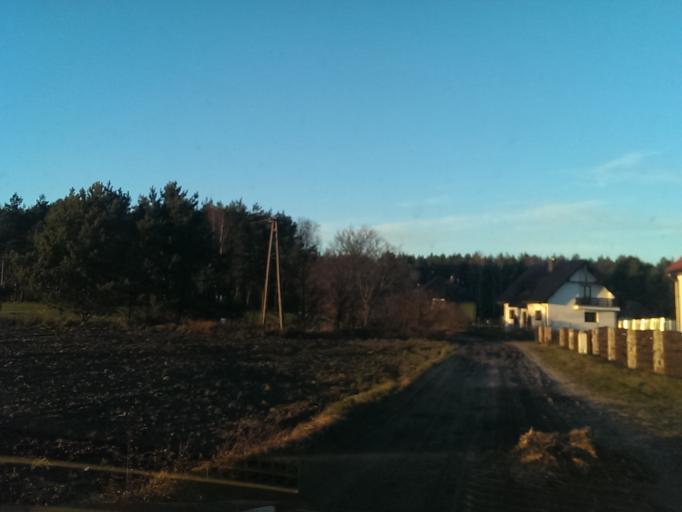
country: PL
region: Kujawsko-Pomorskie
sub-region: Powiat nakielski
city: Szubin
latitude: 53.0600
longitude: 17.6851
